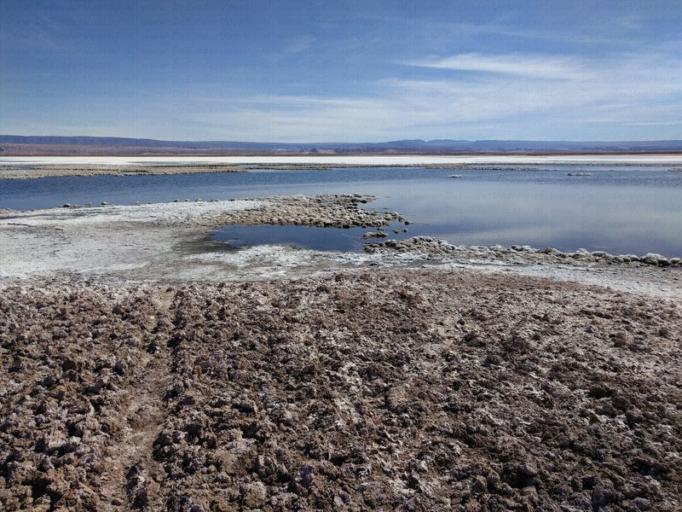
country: CL
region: Antofagasta
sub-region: Provincia de El Loa
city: San Pedro de Atacama
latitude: -23.1382
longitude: -68.2561
